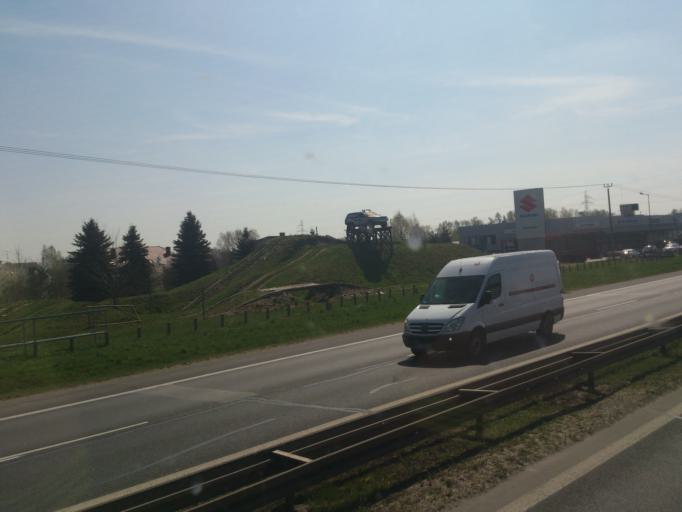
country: PL
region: Lodz Voivodeship
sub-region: Powiat lodzki wschodni
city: Starowa Gora
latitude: 51.6882
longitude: 19.4766
